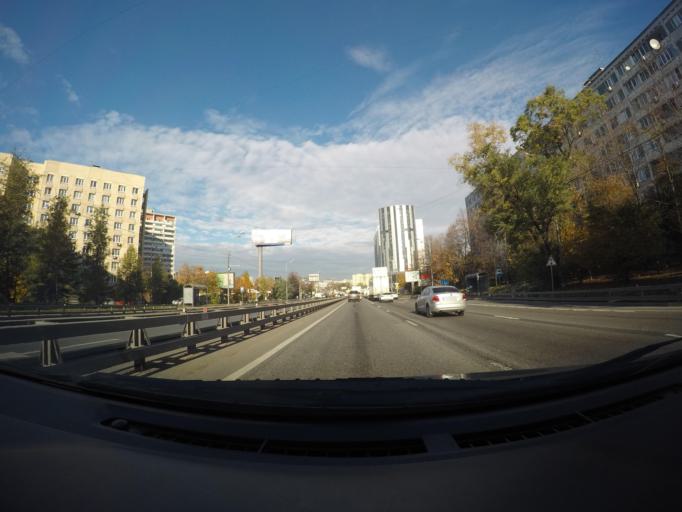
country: RU
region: Moskovskaya
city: Druzhba
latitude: 55.9140
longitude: 37.7736
